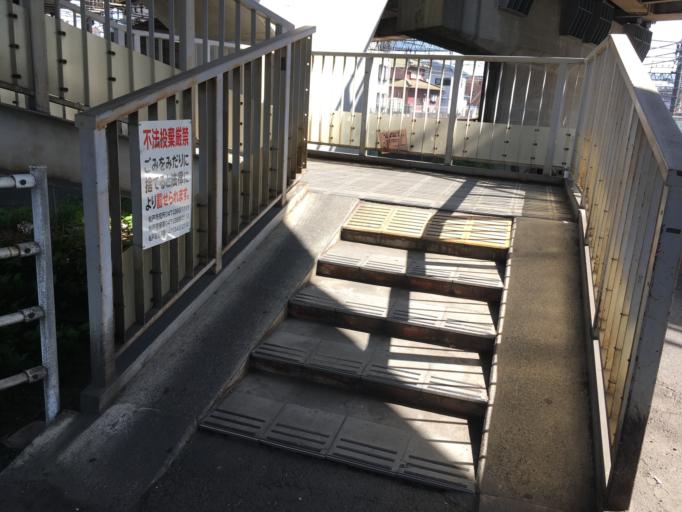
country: JP
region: Chiba
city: Matsudo
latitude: 35.8095
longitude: 139.9163
